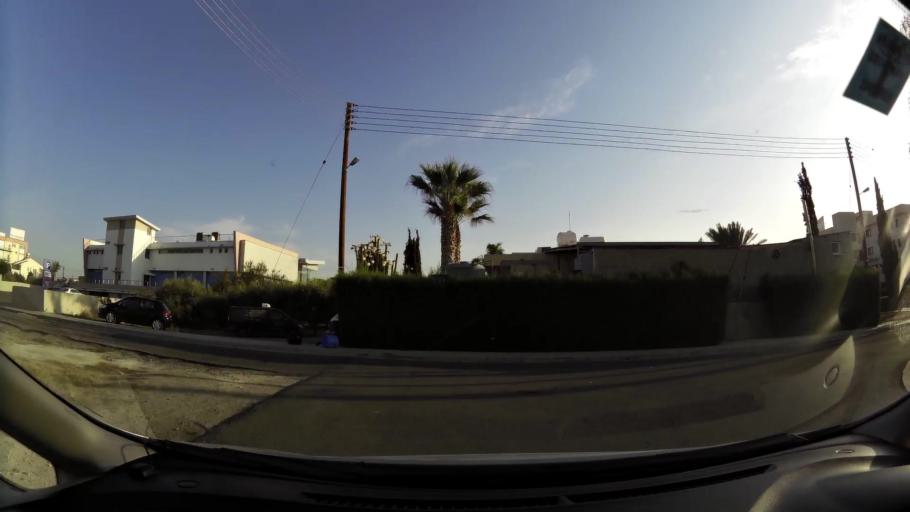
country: CY
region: Larnaka
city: Aradippou
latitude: 34.9328
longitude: 33.5941
